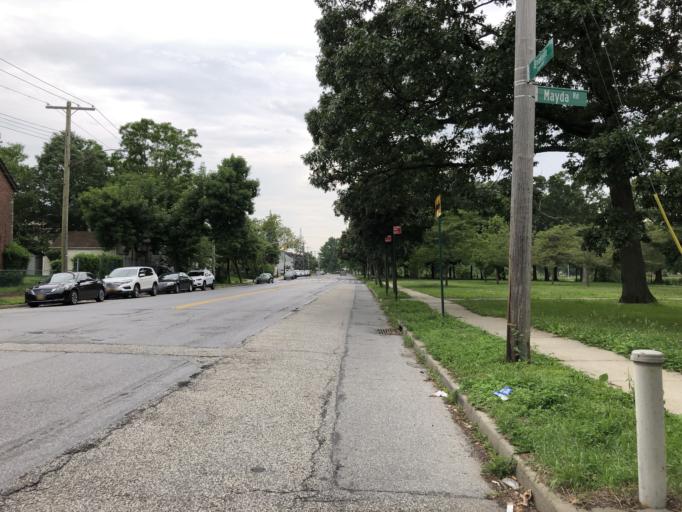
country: US
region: New York
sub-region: Nassau County
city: South Valley Stream
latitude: 40.6604
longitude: -73.7429
